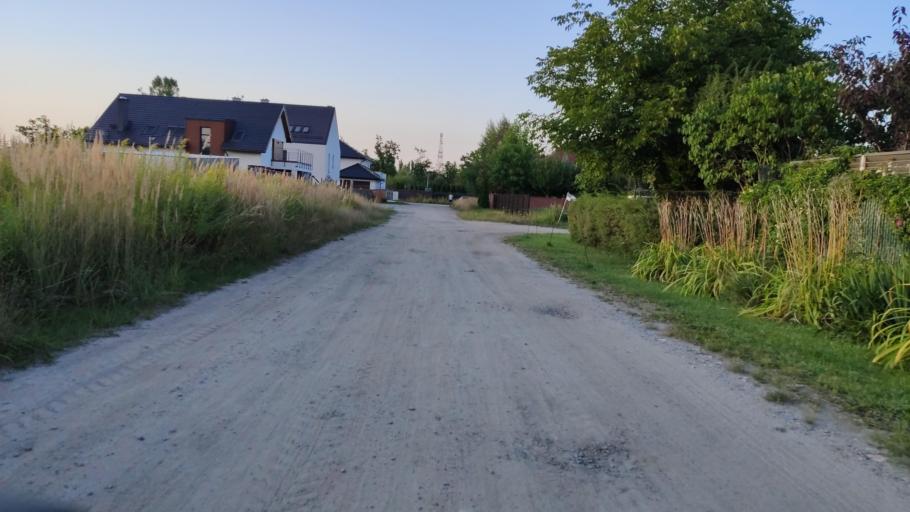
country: PL
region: Lower Silesian Voivodeship
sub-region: Powiat wroclawski
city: Zerniki Wroclawskie
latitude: 51.0641
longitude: 17.0600
